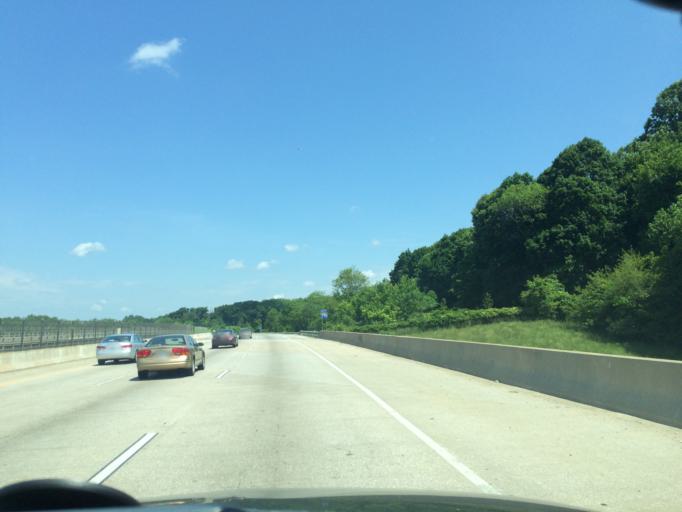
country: US
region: Maryland
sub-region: Baltimore County
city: Garrison
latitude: 39.3804
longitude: -76.7535
